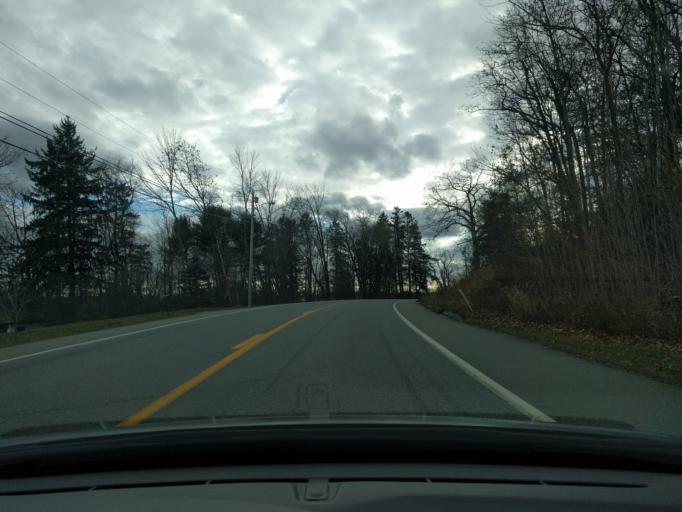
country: US
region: Maine
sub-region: Waldo County
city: Winterport
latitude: 44.6461
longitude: -68.8394
